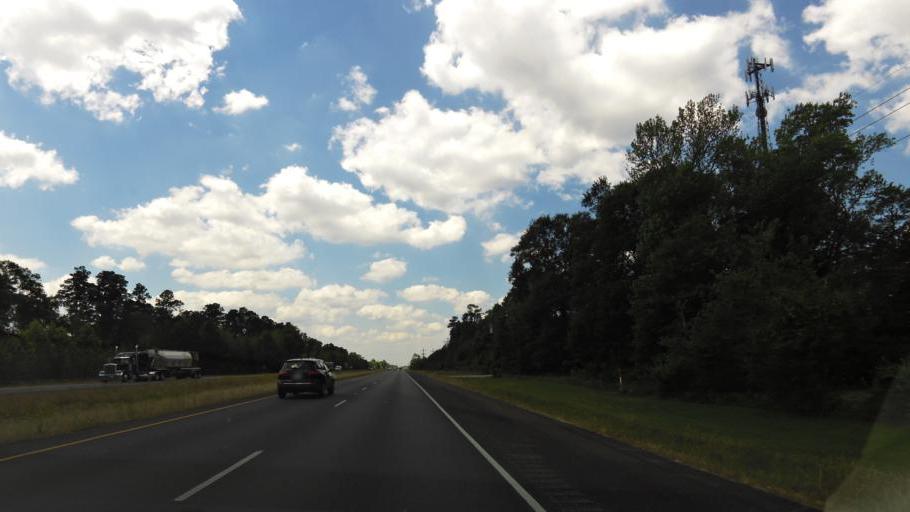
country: US
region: Texas
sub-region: Liberty County
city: Cleveland
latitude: 30.4019
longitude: -95.0549
